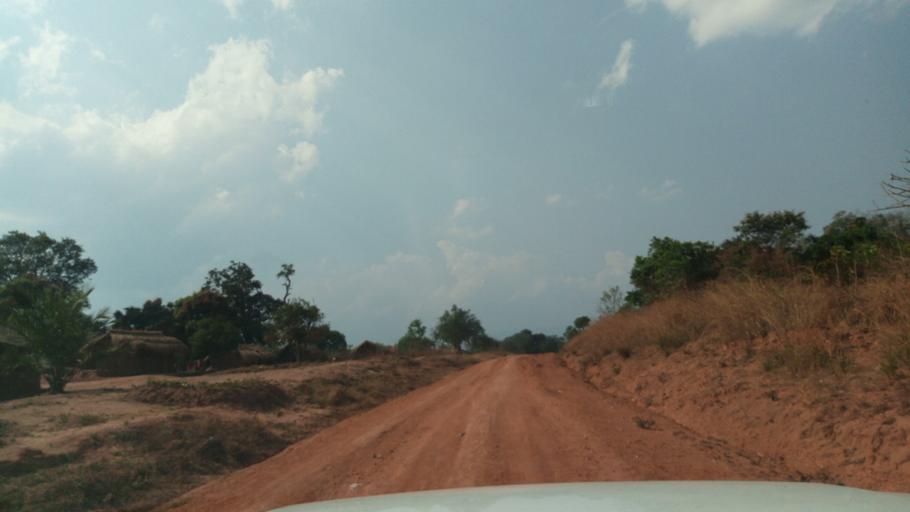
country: CD
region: Katanga
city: Kalemie
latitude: -5.3544
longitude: 28.9395
